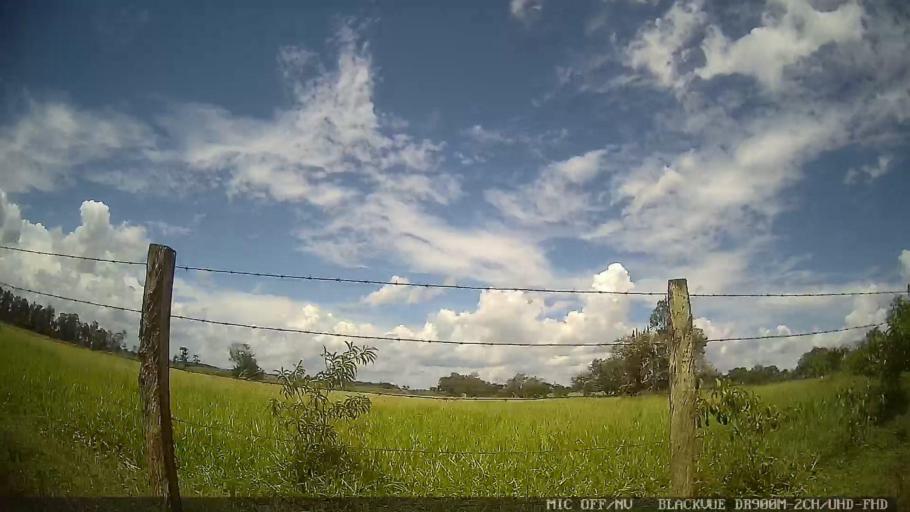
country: BR
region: Sao Paulo
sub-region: Conchas
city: Conchas
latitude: -23.0647
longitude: -47.9779
